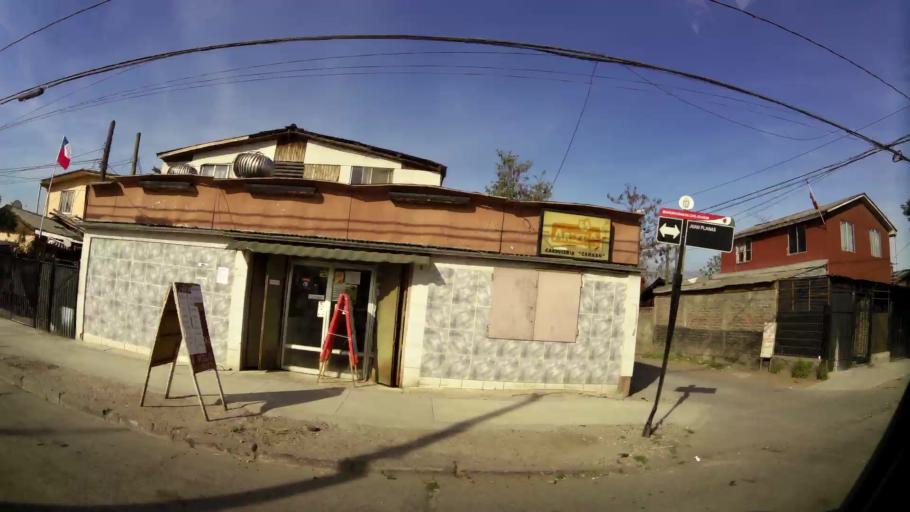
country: CL
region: Santiago Metropolitan
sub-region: Provincia de Santiago
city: Santiago
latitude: -33.5122
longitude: -70.6314
